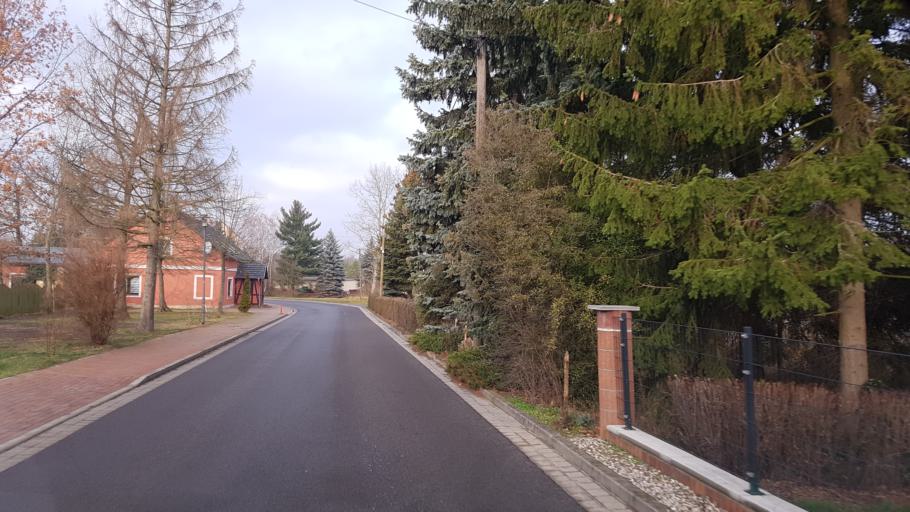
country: DE
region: Brandenburg
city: Sallgast
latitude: 51.5925
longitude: 13.8109
